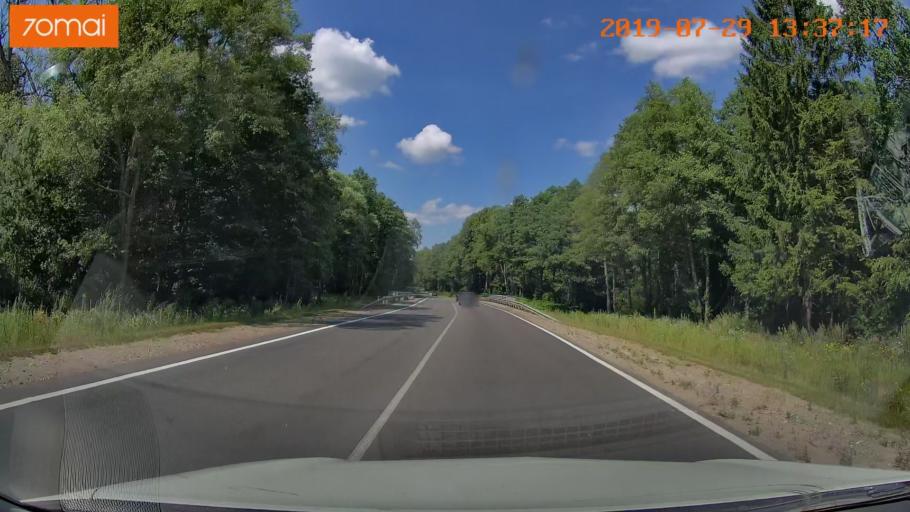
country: RU
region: Kaliningrad
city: Volochayevskoye
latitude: 54.7133
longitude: 20.1865
